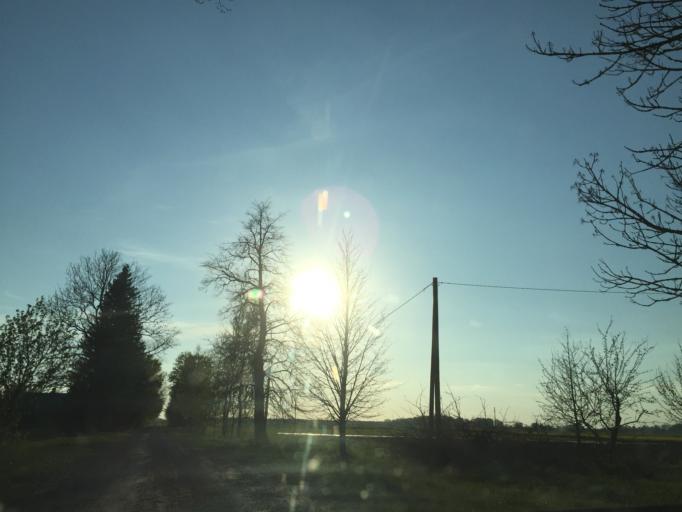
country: LV
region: Bauskas Rajons
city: Bauska
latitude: 56.2964
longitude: 24.2833
